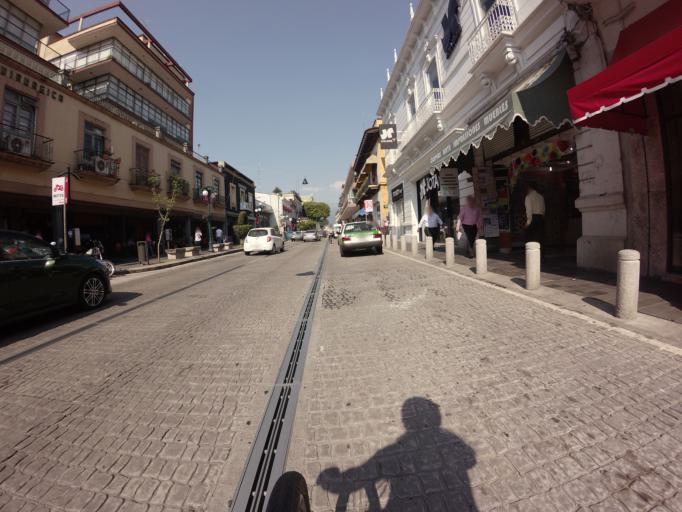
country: MX
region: Veracruz
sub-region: Xalapa
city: Xalapa de Enriquez
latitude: 19.5300
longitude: -96.9229
